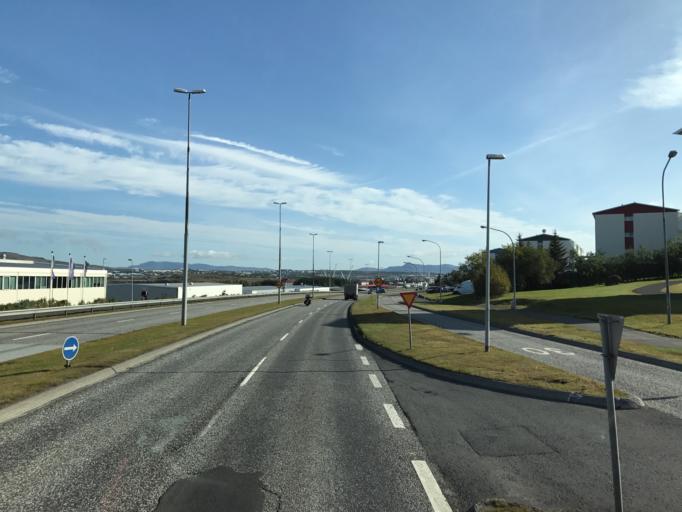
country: IS
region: Capital Region
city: Reykjavik
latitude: 64.1487
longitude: -21.8659
